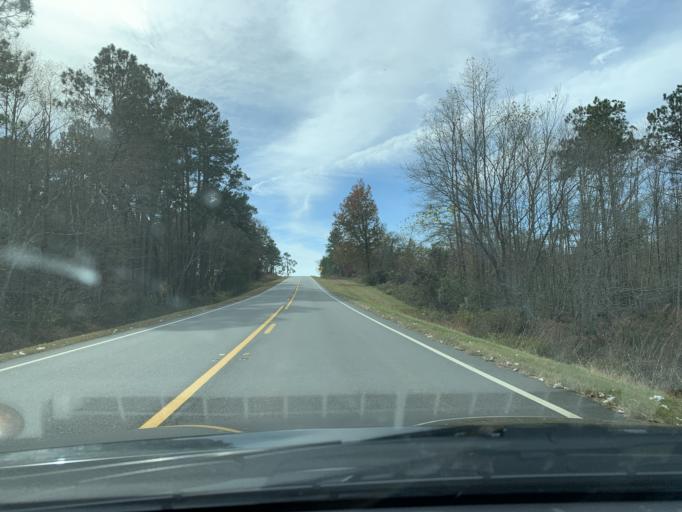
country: US
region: Georgia
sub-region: Wilcox County
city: Rochelle
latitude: 31.7891
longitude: -83.5048
